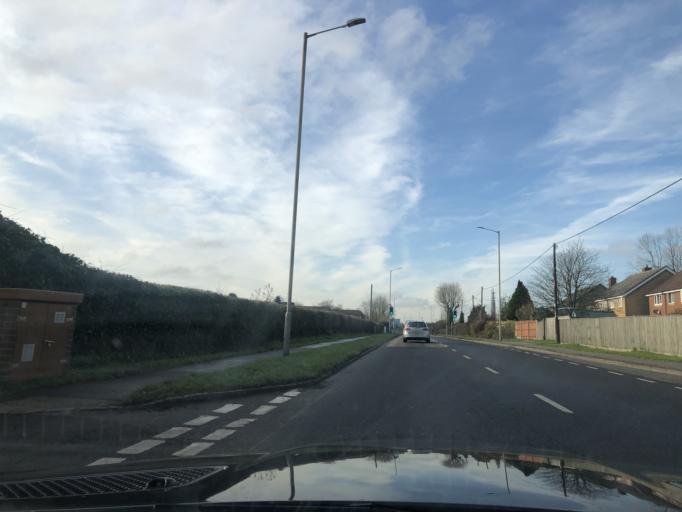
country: GB
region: England
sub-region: Buckinghamshire
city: Stokenchurch
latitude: 51.6610
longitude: -0.9063
